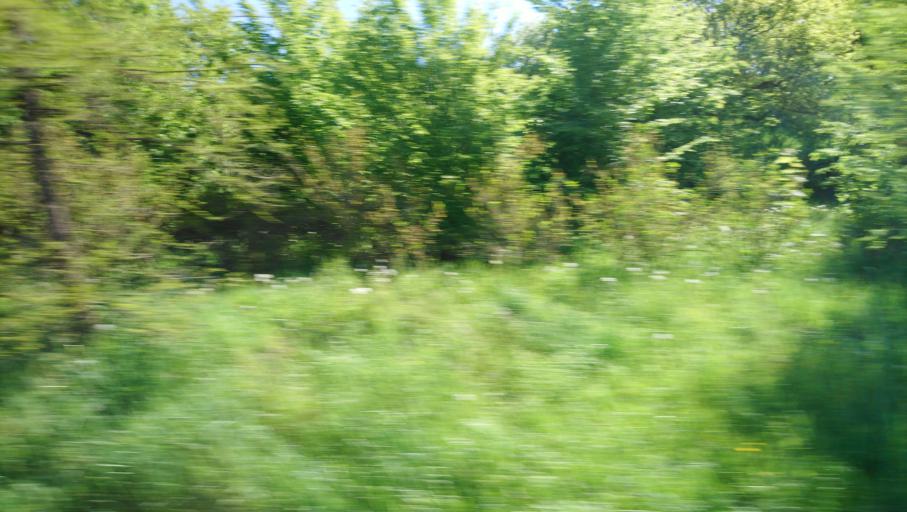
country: LU
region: Diekirch
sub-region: Canton de Vianden
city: Tandel
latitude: 49.8778
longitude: 6.1888
